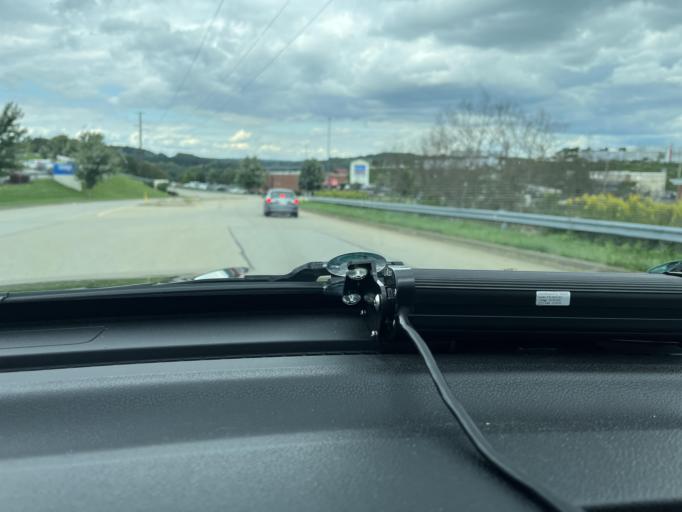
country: US
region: Pennsylvania
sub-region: Fayette County
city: South Uniontown
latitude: 39.9144
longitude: -79.7533
